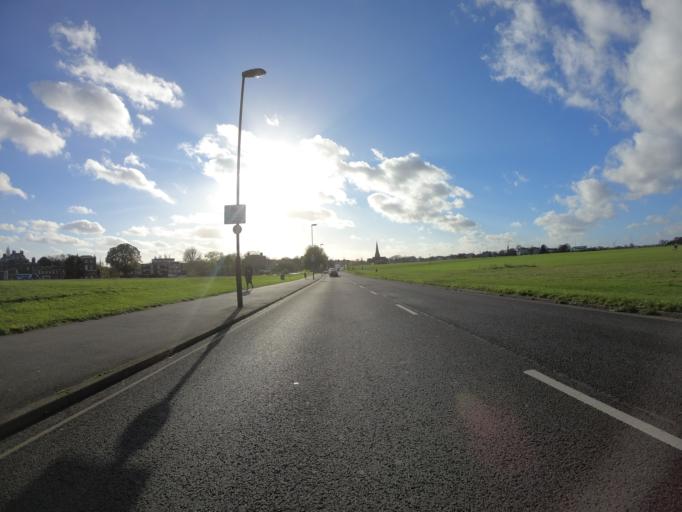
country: GB
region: England
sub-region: Greater London
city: Blackheath
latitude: 51.4713
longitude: 0.0124
